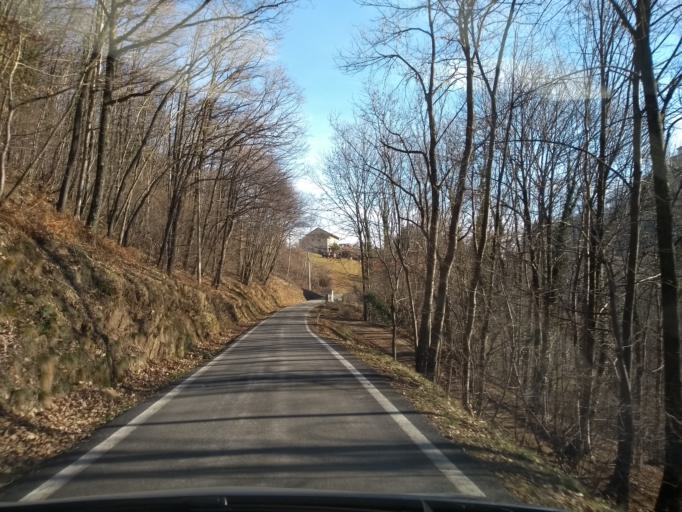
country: IT
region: Piedmont
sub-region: Provincia di Torino
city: Traves
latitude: 45.2812
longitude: 7.4389
